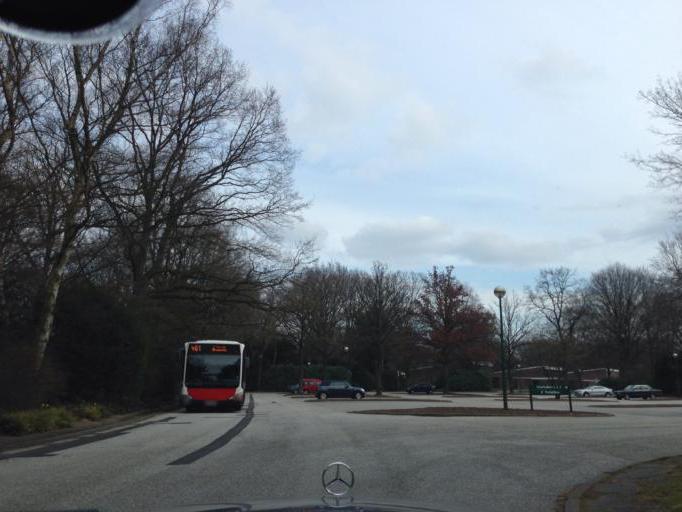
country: DE
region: Hamburg
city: Wandsbek
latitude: 53.5573
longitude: 10.1249
